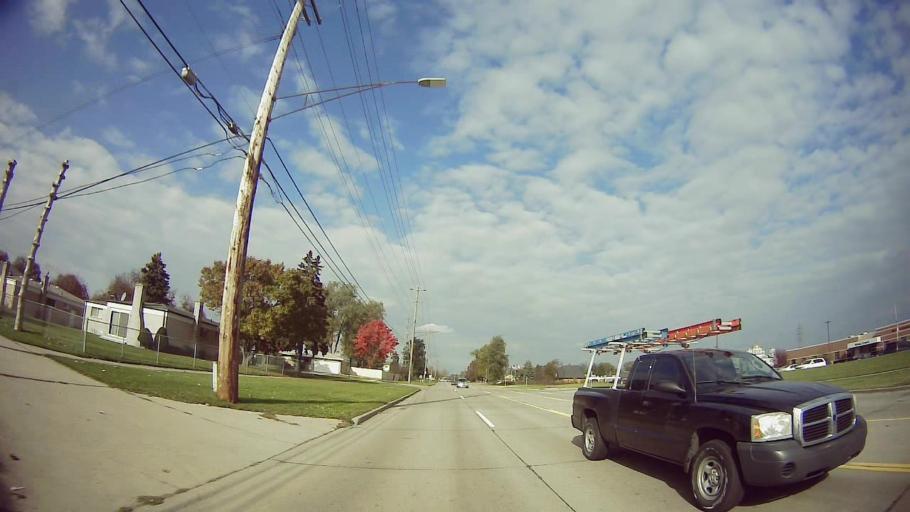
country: US
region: Michigan
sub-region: Oakland County
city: Madison Heights
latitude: 42.5223
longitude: -83.0681
